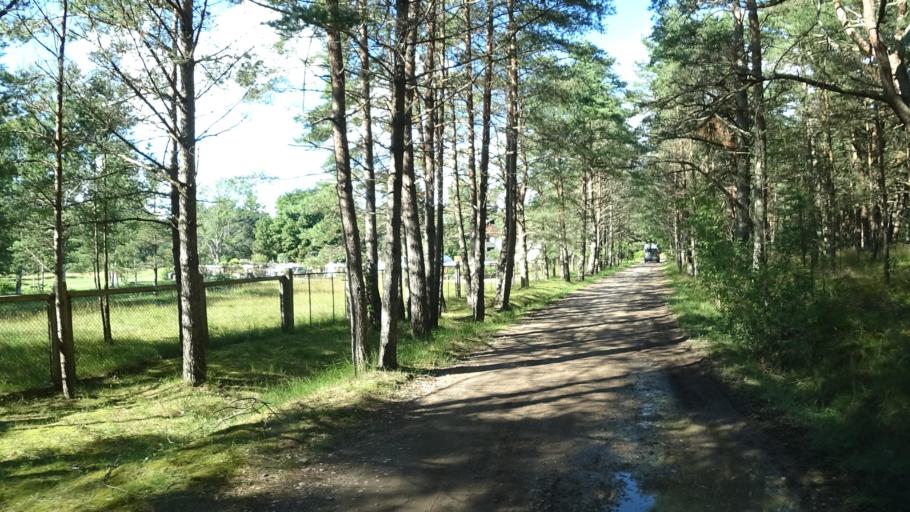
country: LV
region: Ventspils
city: Ventspils
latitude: 57.4882
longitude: 21.6479
